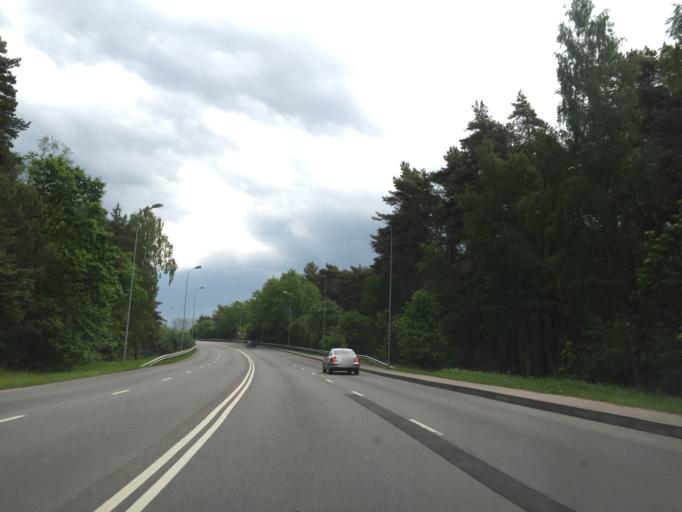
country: LT
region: Klaipedos apskritis
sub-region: Klaipeda
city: Klaipeda
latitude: 55.7351
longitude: 21.1014
